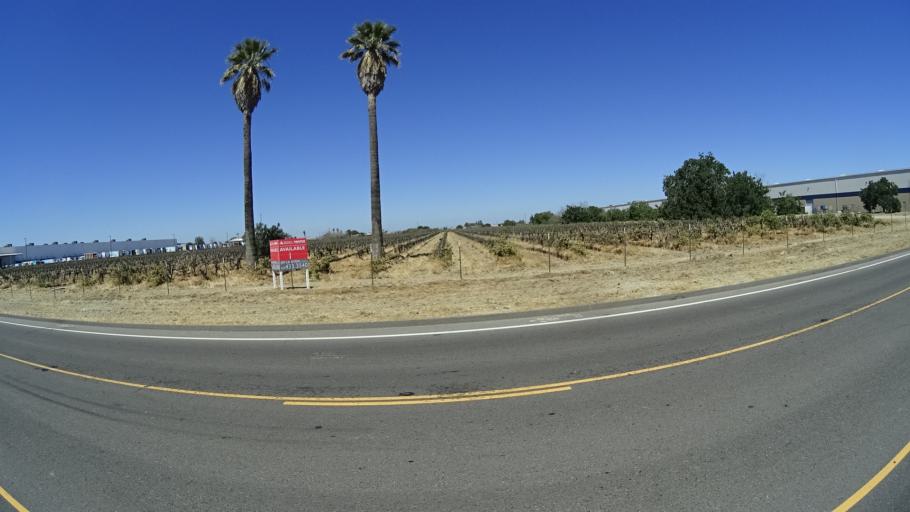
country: US
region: California
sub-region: Fresno County
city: Easton
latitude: 36.6861
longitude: -119.7726
